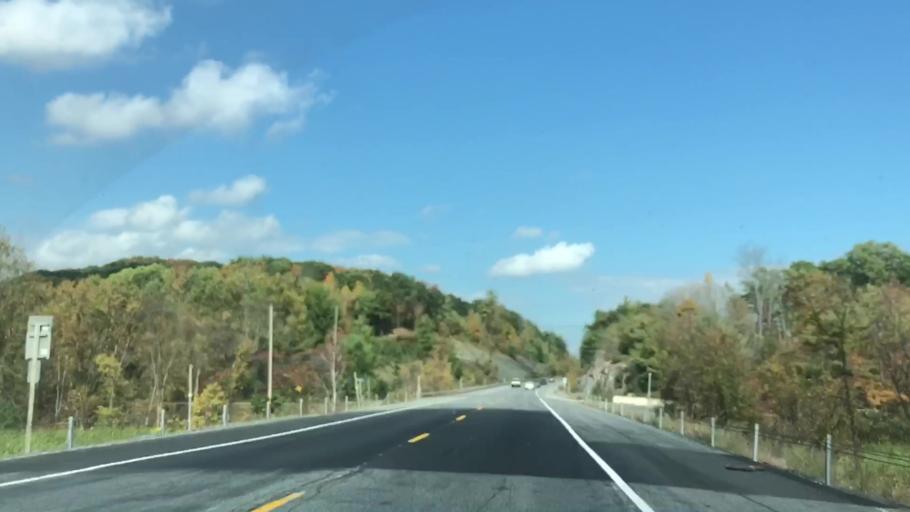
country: US
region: New York
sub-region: Washington County
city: Whitehall
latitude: 43.4502
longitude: -73.4495
